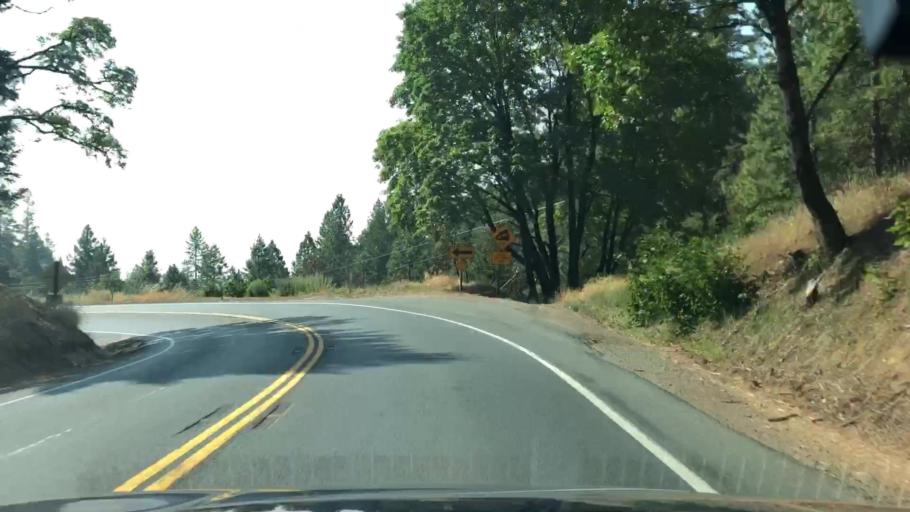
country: US
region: California
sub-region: Napa County
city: Calistoga
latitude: 38.6515
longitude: -122.5998
